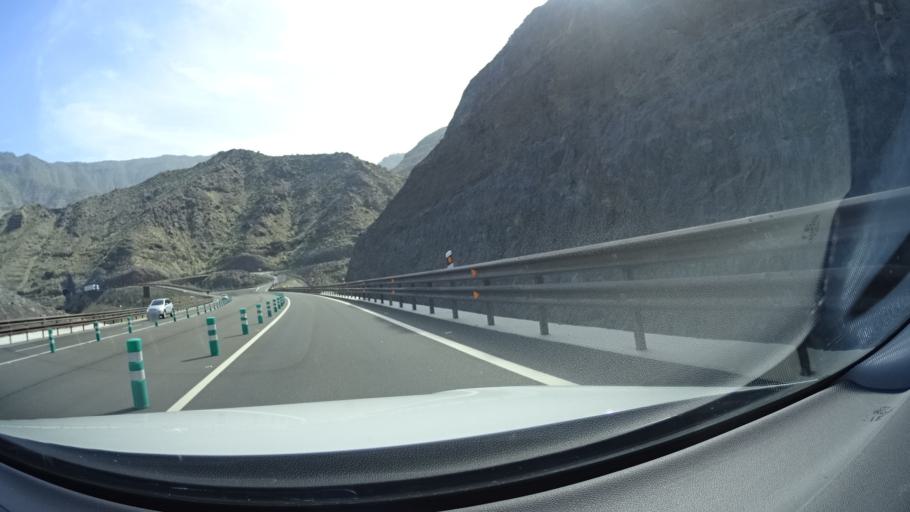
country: ES
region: Canary Islands
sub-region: Provincia de Las Palmas
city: San Nicolas
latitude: 28.0401
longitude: -15.7384
